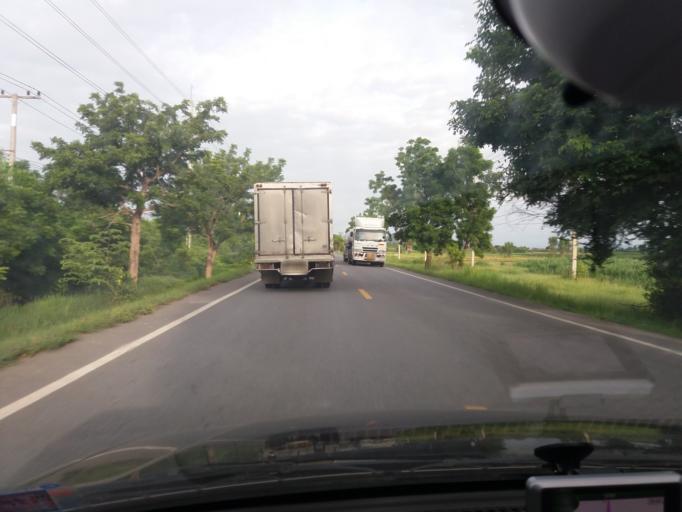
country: TH
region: Kanchanaburi
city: Huai Krachao
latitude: 14.3322
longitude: 99.7354
